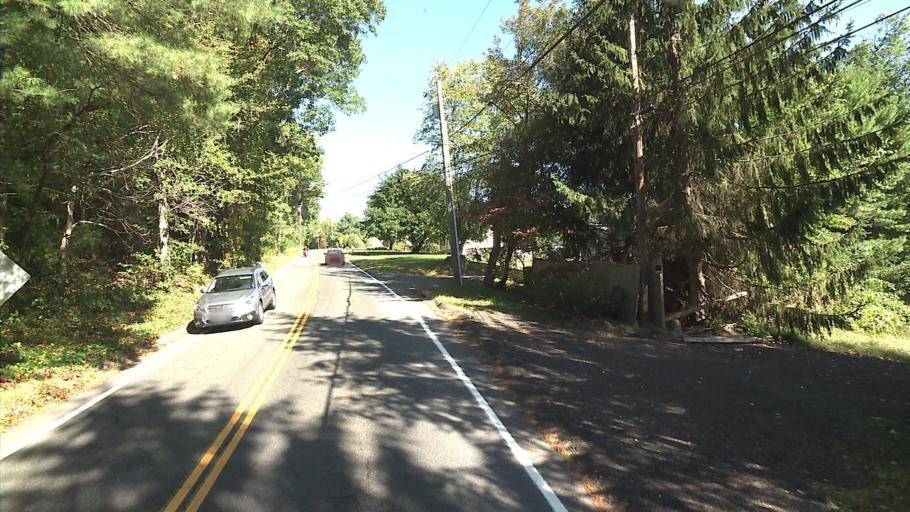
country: US
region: Connecticut
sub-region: Hartford County
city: Bristol
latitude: 41.7266
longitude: -72.9498
